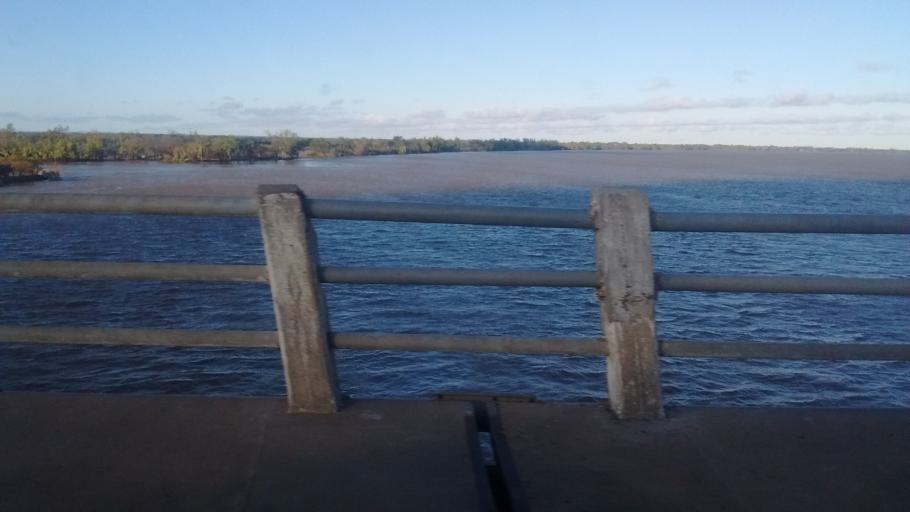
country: AR
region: Entre Rios
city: Parana
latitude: -31.6604
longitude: -60.5971
